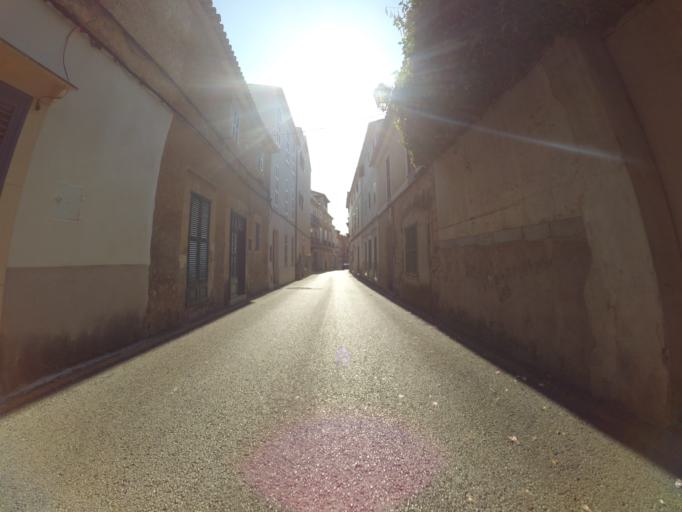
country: ES
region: Balearic Islands
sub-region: Illes Balears
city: Arta
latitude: 39.6957
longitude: 3.3487
